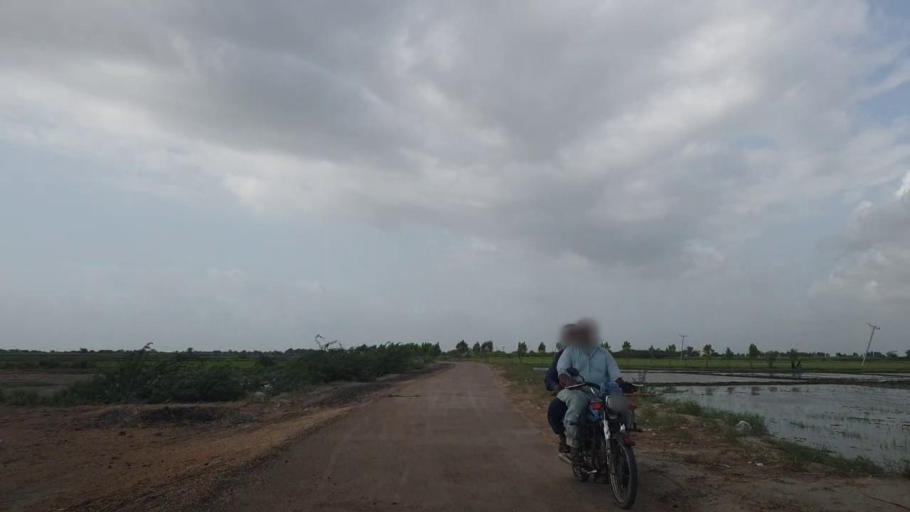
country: PK
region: Sindh
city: Kadhan
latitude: 24.5908
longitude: 69.0550
